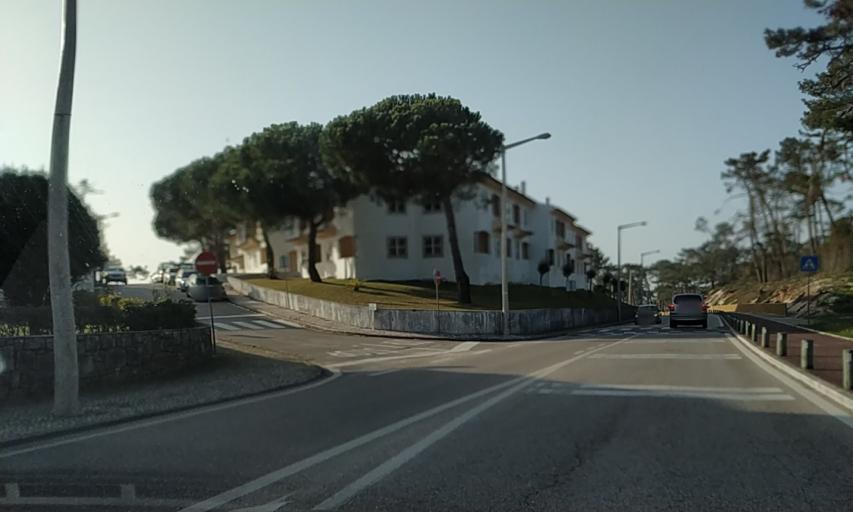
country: PT
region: Leiria
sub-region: Alcobaca
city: Pataias
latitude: 39.7556
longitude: -9.0255
